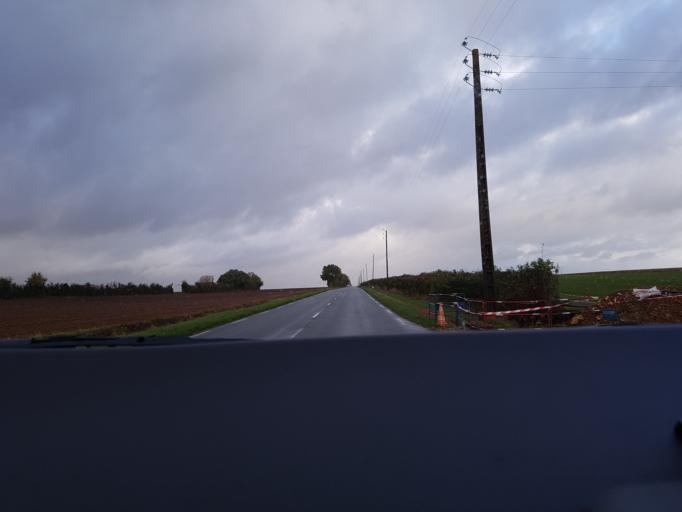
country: FR
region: Poitou-Charentes
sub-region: Departement des Deux-Sevres
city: Brioux-sur-Boutonne
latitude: 46.1641
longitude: -0.2018
